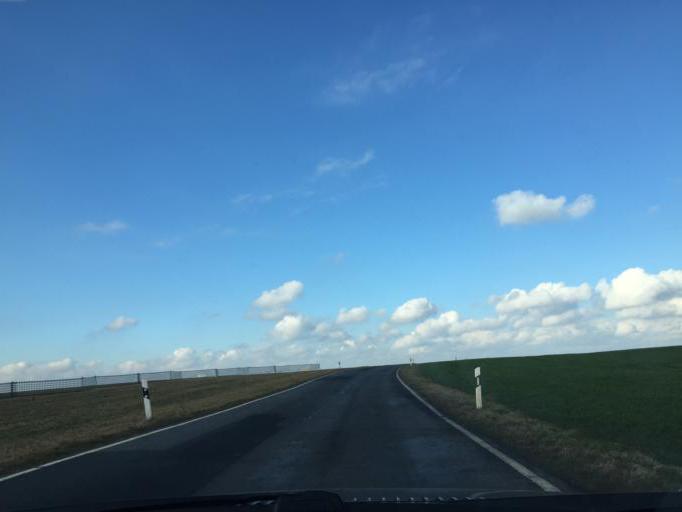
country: DE
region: Saxony
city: Tauscha
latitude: 51.2627
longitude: 13.7683
